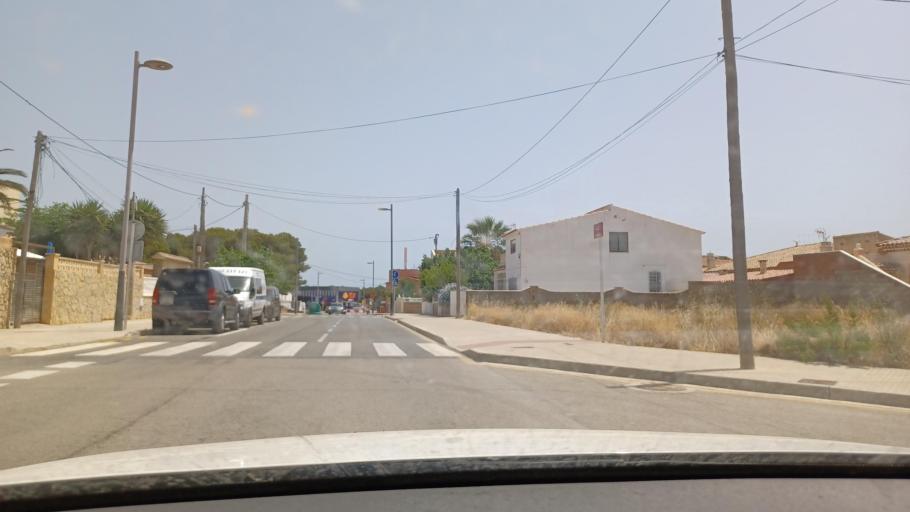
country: ES
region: Catalonia
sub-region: Provincia de Tarragona
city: Colldejou
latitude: 41.0016
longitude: 0.9281
